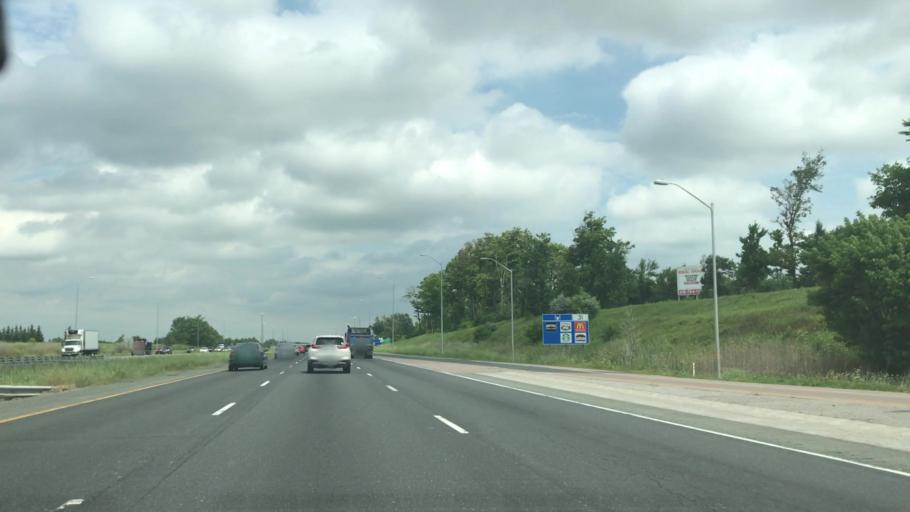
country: CA
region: Ontario
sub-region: York
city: Richmond Hill
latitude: 43.8688
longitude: -79.3761
